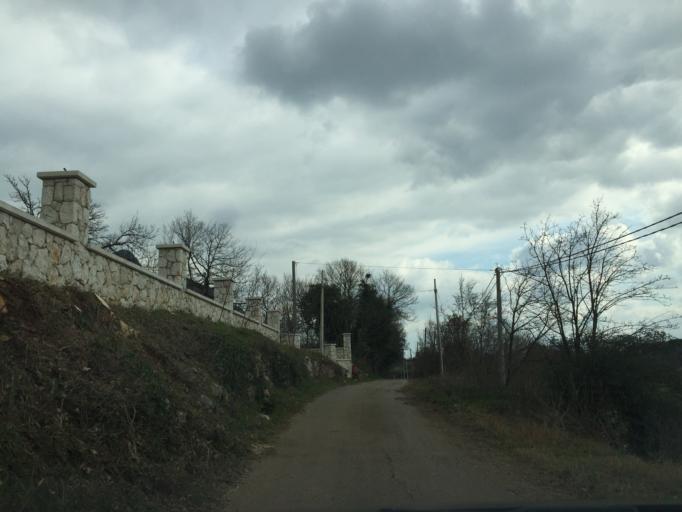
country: IT
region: Latium
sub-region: Provincia di Frosinone
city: Villa Santa Lucia
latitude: 41.4888
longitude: 13.7876
